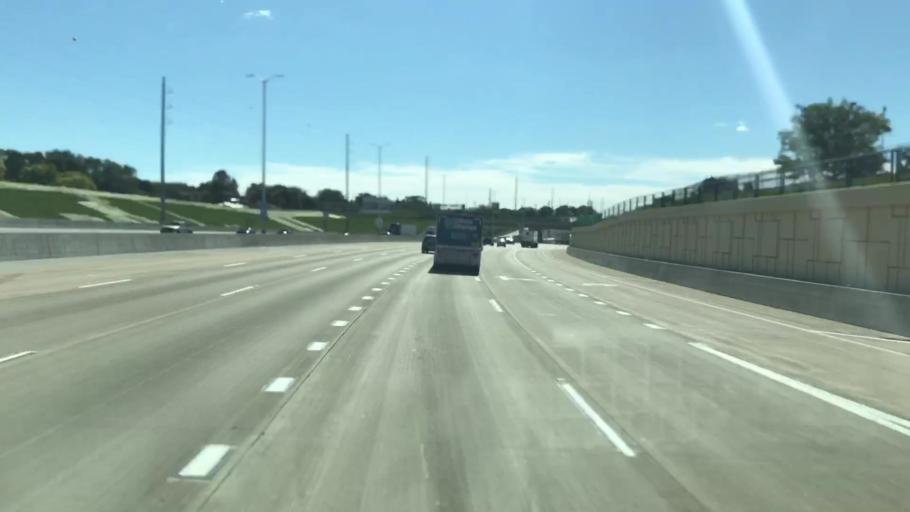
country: US
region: Wisconsin
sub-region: Milwaukee County
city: Wauwatosa
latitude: 43.0414
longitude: -88.0335
